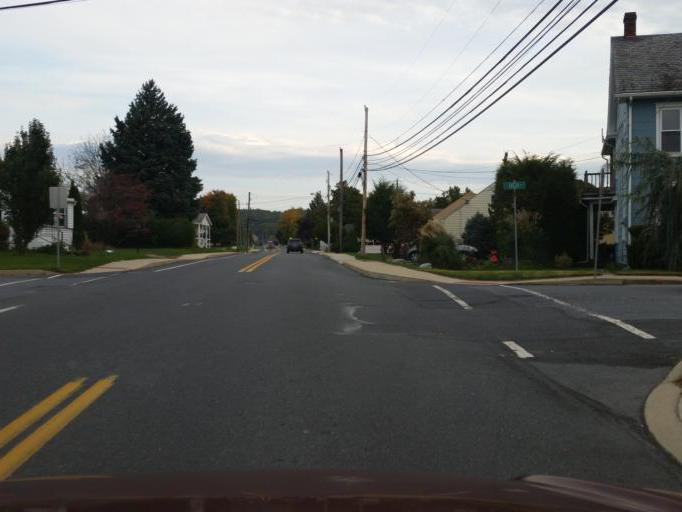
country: US
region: Pennsylvania
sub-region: Dauphin County
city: Hummelstown
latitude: 40.2644
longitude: -76.7034
